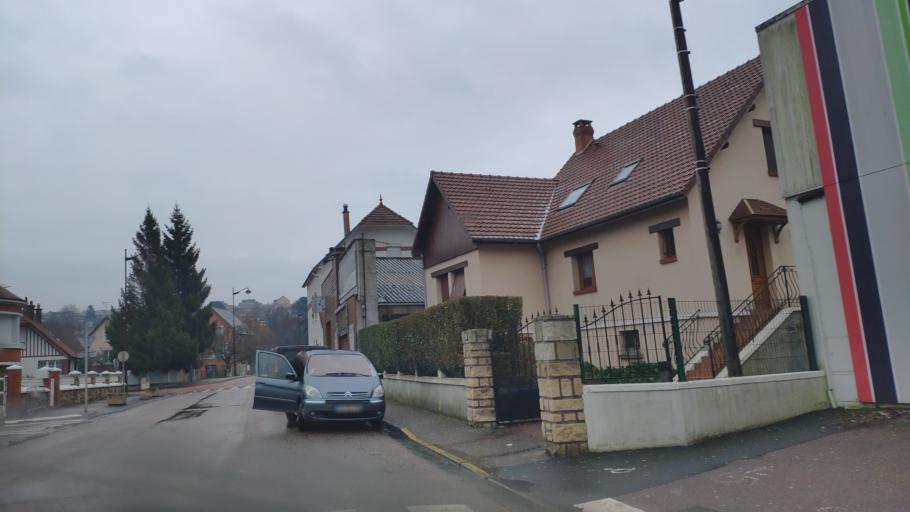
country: FR
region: Haute-Normandie
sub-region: Departement de la Seine-Maritime
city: Cany-Barville
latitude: 49.7881
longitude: 0.6354
